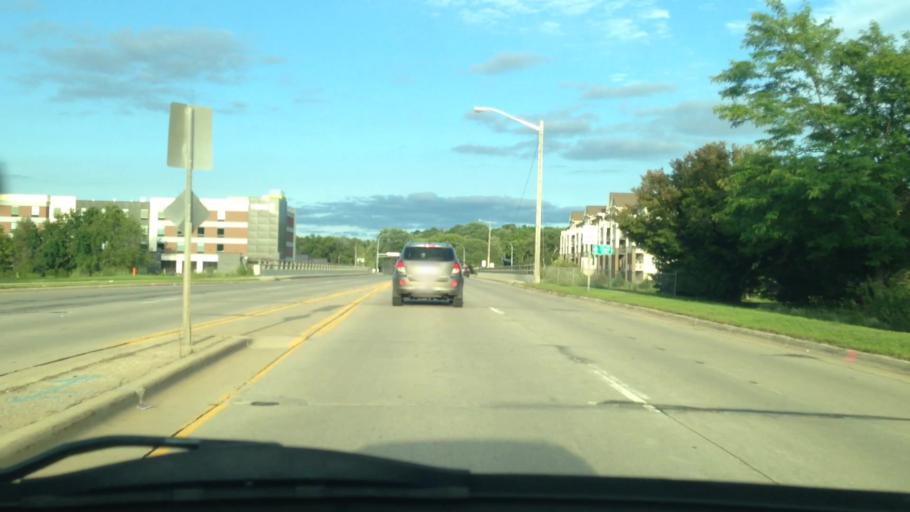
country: US
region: Minnesota
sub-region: Olmsted County
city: Rochester
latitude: 44.0007
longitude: -92.4788
